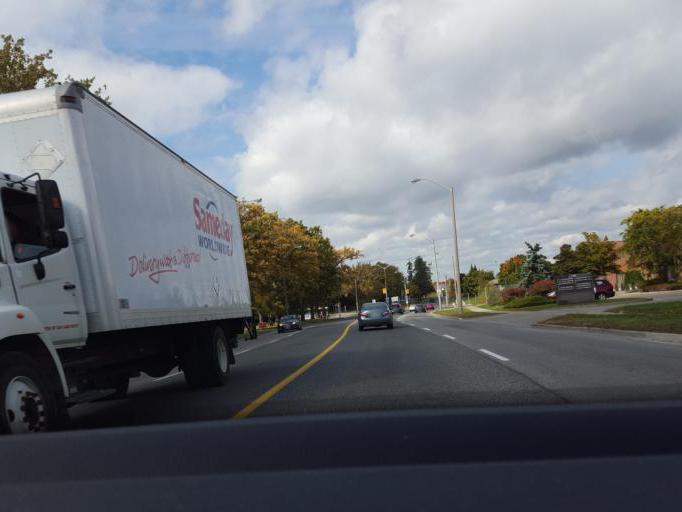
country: CA
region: Ontario
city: Scarborough
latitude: 43.8074
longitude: -79.2018
